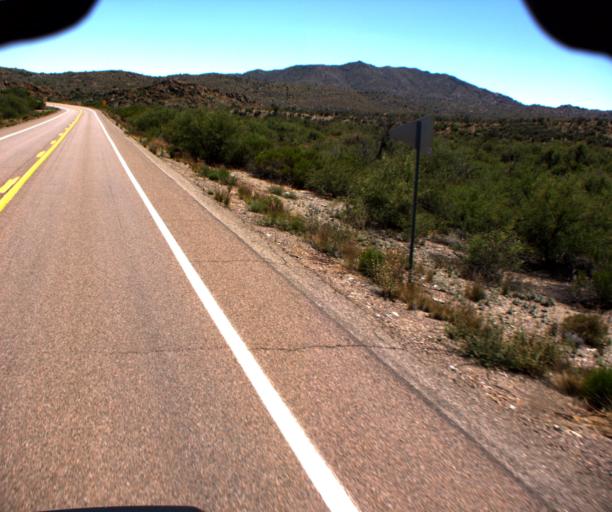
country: US
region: Arizona
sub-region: Yavapai County
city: Bagdad
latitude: 34.5292
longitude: -113.1367
